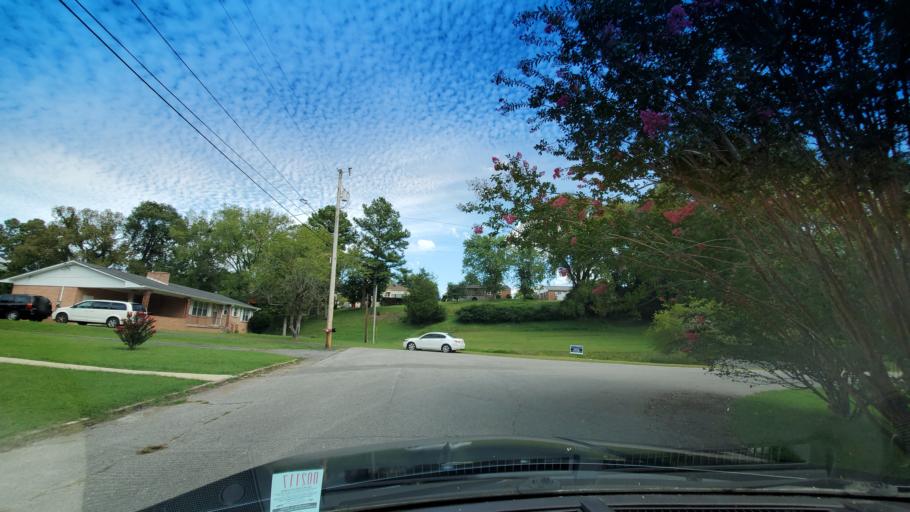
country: US
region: Tennessee
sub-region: Smith County
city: Carthage
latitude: 36.2552
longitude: -85.9446
